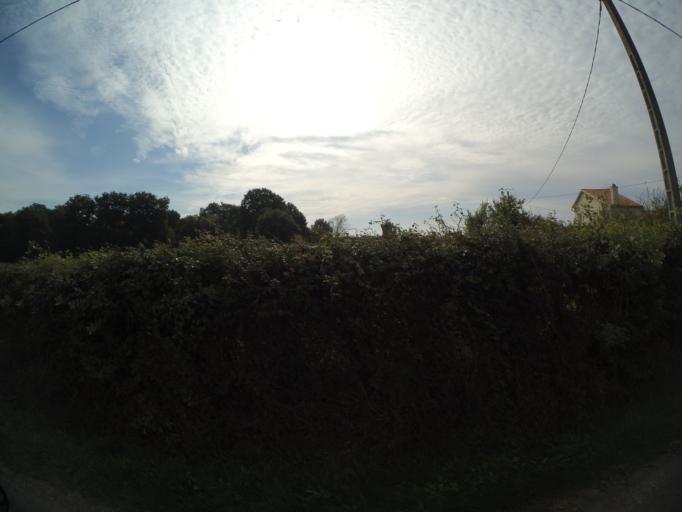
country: FR
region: Pays de la Loire
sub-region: Departement de Maine-et-Loire
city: La Jubaudiere
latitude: 47.1847
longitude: -0.9163
